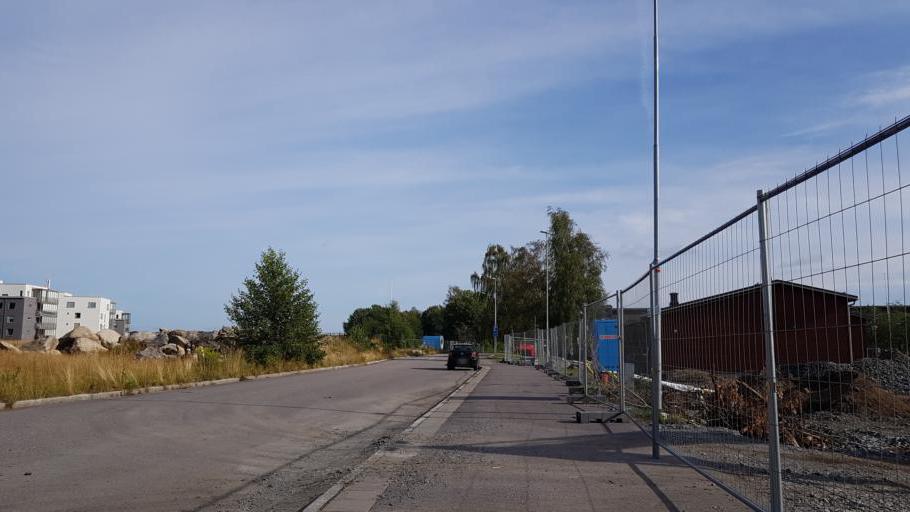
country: SE
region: Vaestra Goetaland
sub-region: Molndal
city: Moelndal
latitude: 57.6657
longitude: 12.0357
